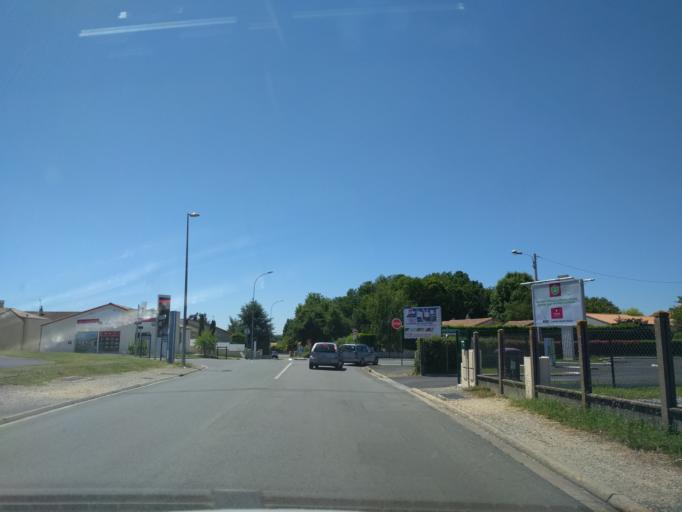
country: FR
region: Poitou-Charentes
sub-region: Departement des Deux-Sevres
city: Niort
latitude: 46.3334
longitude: -0.4219
